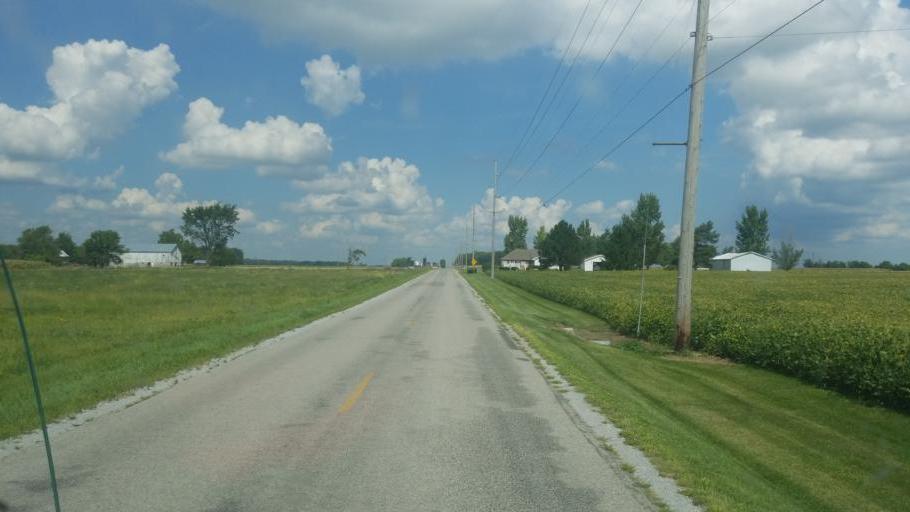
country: US
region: Ohio
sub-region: Hardin County
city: Kenton
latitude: 40.7287
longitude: -83.6529
